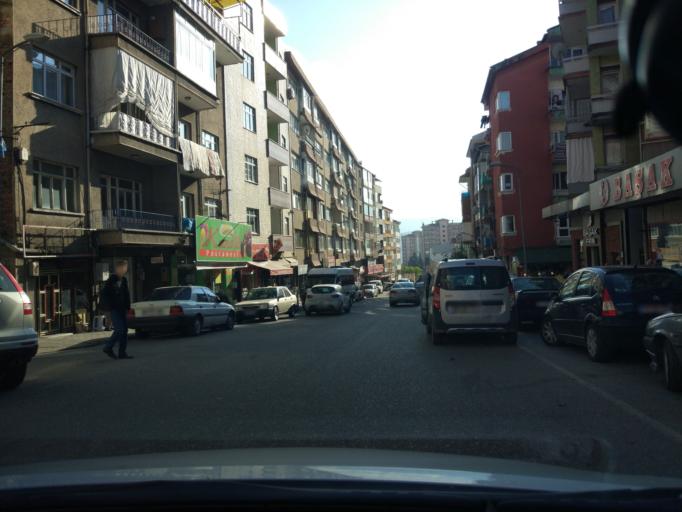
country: TR
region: Karabuk
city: Karabuk
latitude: 41.2062
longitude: 32.6266
